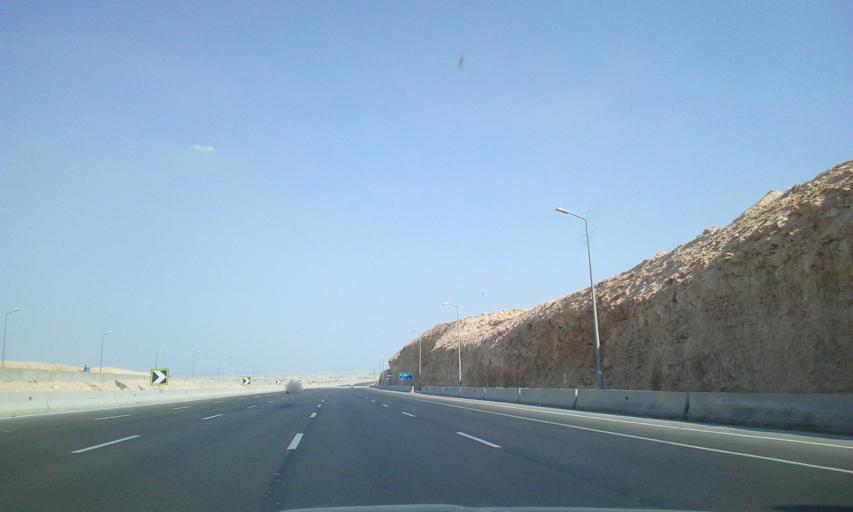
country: EG
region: As Suways
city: Ain Sukhna
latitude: 29.6816
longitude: 32.2150
